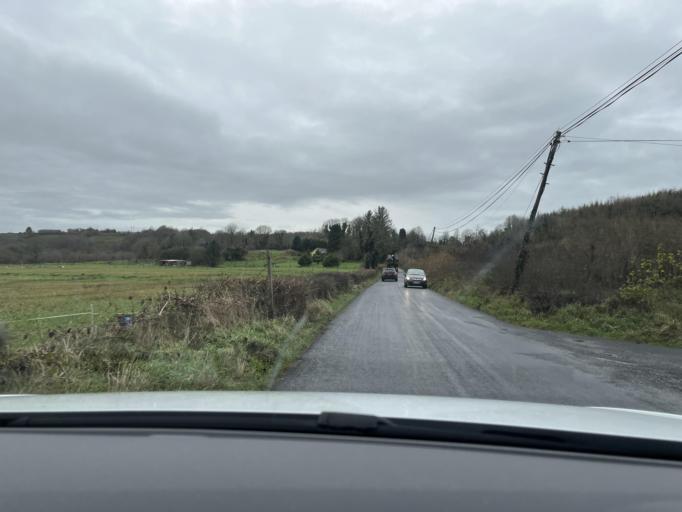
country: IE
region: Connaught
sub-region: County Leitrim
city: Manorhamilton
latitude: 54.2387
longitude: -8.2724
